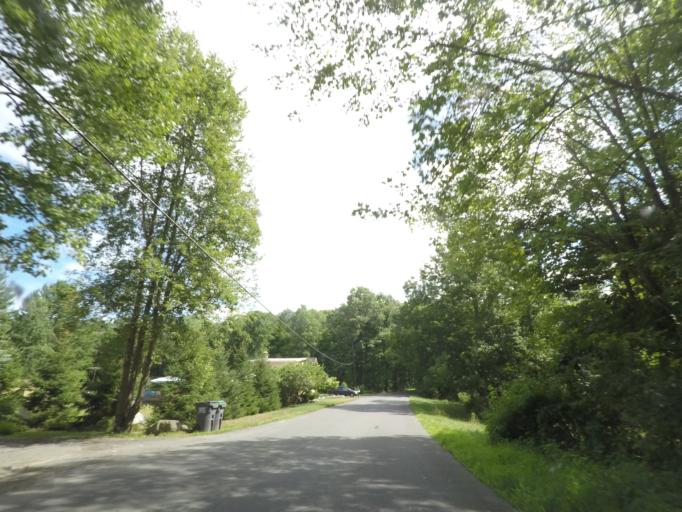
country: US
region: New York
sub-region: Rensselaer County
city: Averill Park
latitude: 42.6507
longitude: -73.5494
